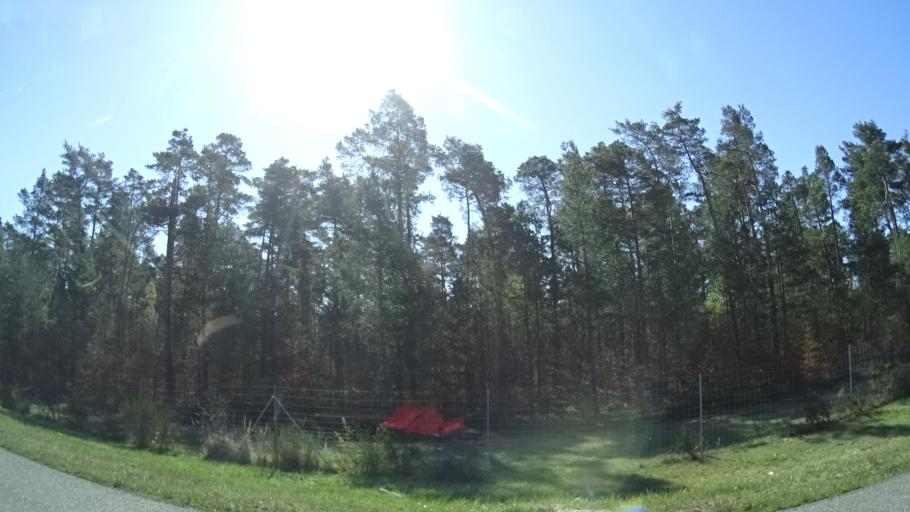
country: DE
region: Bavaria
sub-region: Regierungsbezirk Mittelfranken
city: Feucht
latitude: 49.3960
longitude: 11.2037
